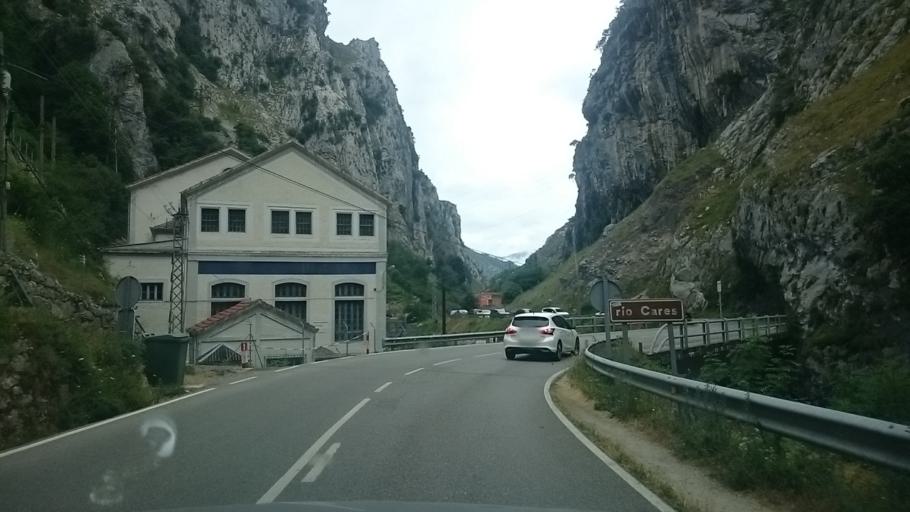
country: ES
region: Asturias
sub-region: Province of Asturias
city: Carrena
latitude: 43.2592
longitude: -4.8308
